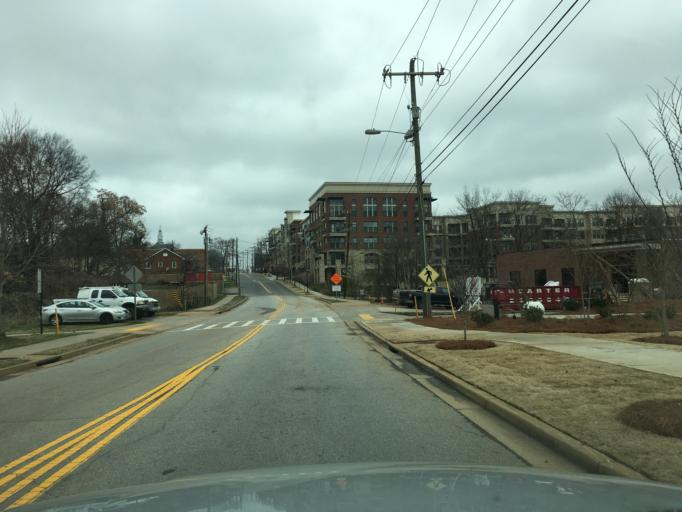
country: US
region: South Carolina
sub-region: Greenville County
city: Greenville
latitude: 34.8480
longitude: -82.4071
